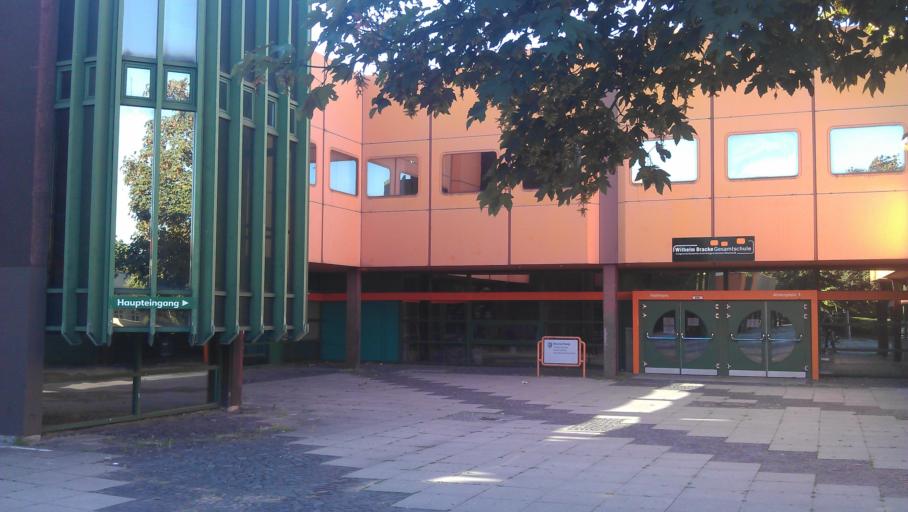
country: DE
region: Lower Saxony
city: Braunschweig
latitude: 52.2513
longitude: 10.4783
